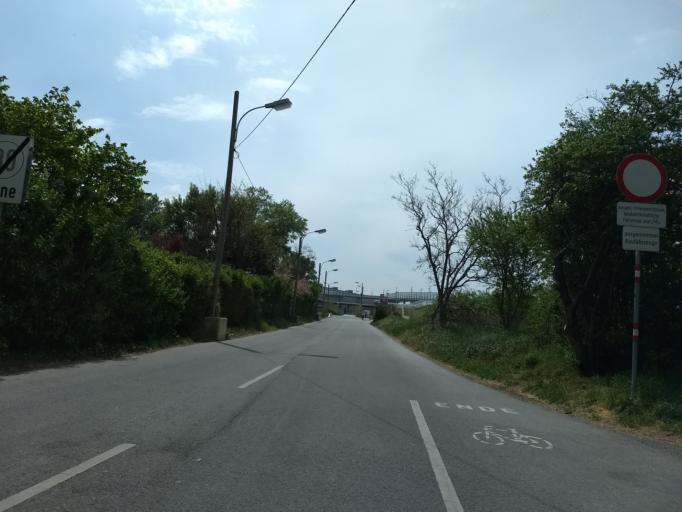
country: AT
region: Lower Austria
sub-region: Politischer Bezirk Ganserndorf
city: Aderklaa
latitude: 48.2368
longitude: 16.5042
